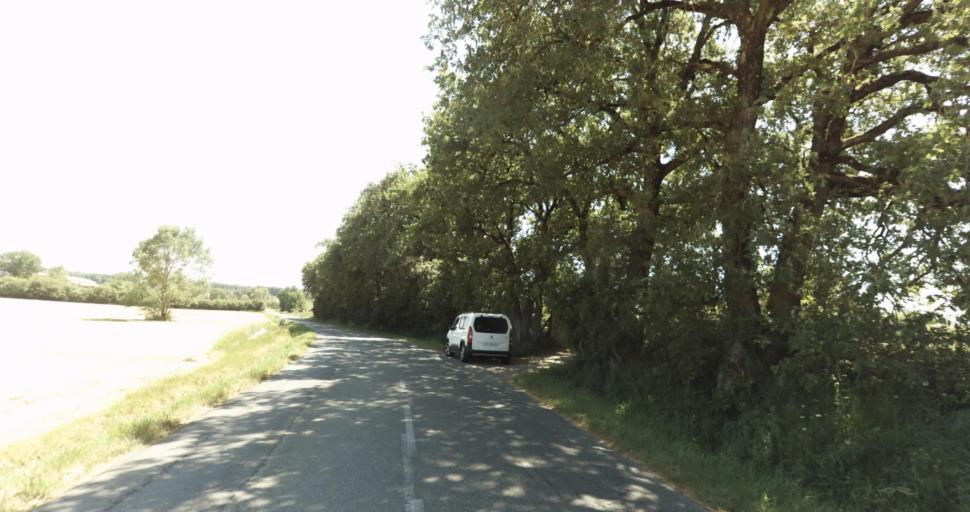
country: FR
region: Midi-Pyrenees
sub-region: Departement de la Haute-Garonne
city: Levignac
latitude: 43.6310
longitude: 1.1813
